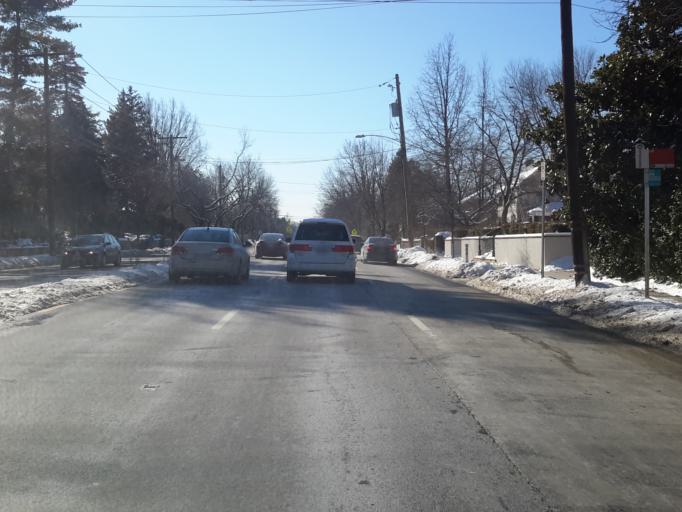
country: US
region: Maryland
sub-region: Montgomery County
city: Chevy Chase
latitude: 38.9799
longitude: -77.0772
